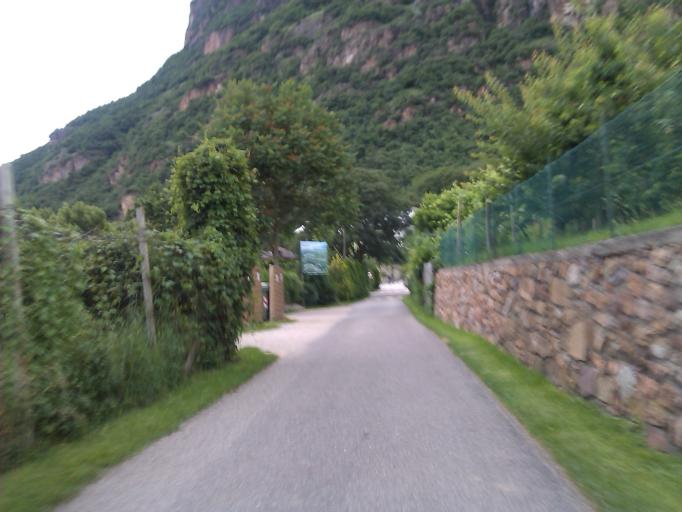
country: IT
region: Trentino-Alto Adige
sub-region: Bolzano
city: Bolzano
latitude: 46.5023
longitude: 11.3002
